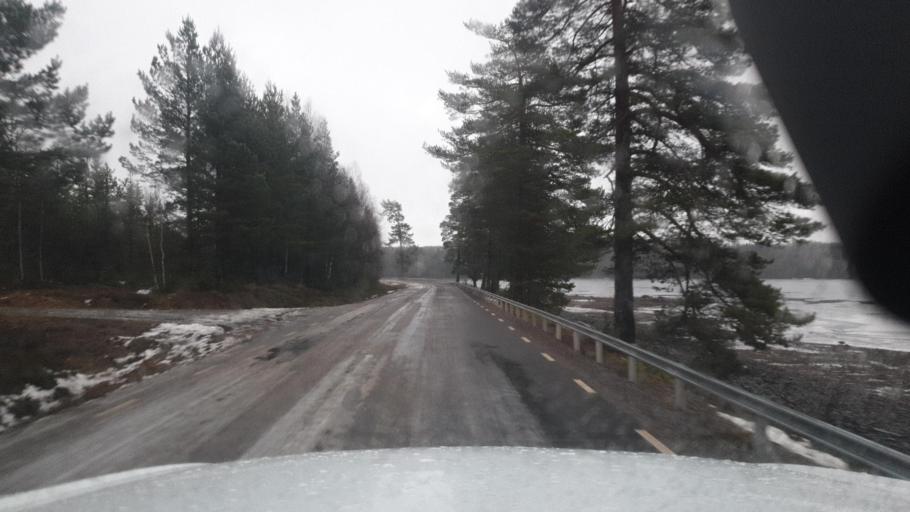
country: SE
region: Vaermland
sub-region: Torsby Kommun
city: Torsby
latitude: 59.9813
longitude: 12.7940
